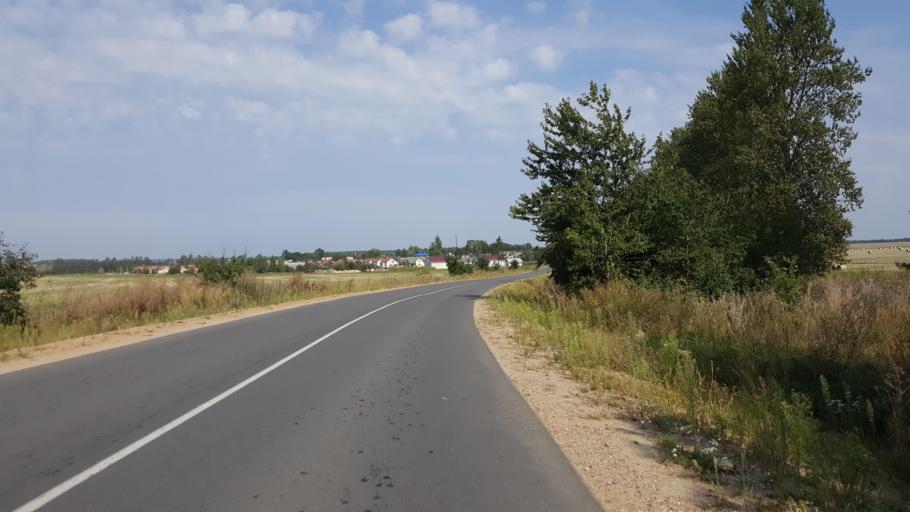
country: BY
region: Brest
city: Kamyanyets
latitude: 52.4598
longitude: 23.7345
